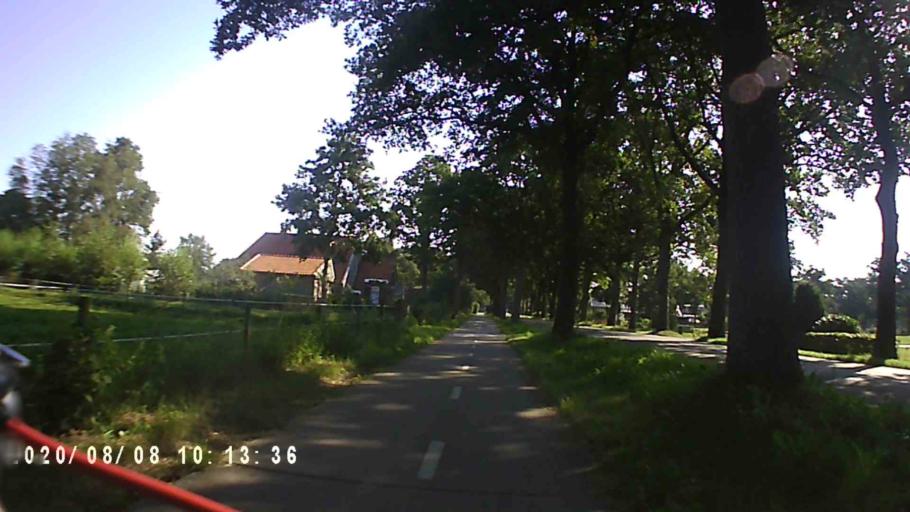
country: NL
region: Groningen
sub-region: Gemeente Leek
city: Leek
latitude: 53.1268
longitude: 6.3896
